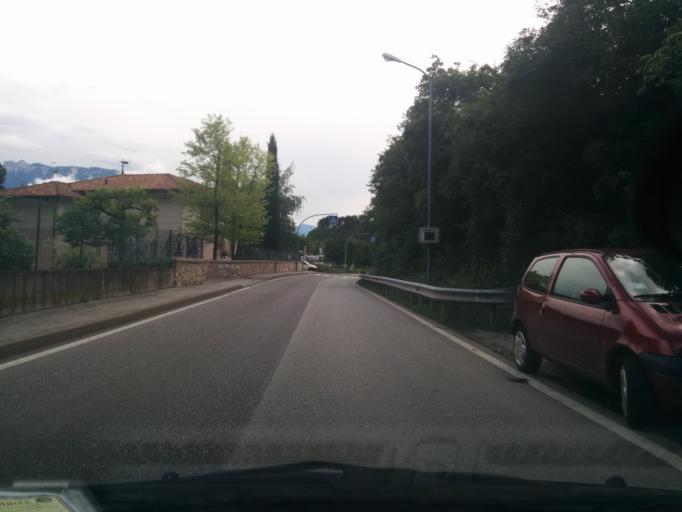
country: IT
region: Trentino-Alto Adige
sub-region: Provincia di Trento
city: Trento
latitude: 46.0901
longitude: 11.1336
